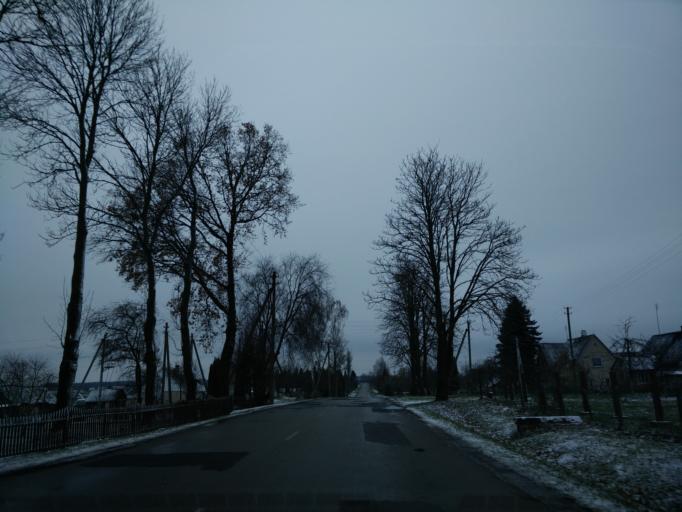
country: LT
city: Ariogala
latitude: 55.4237
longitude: 23.3470
